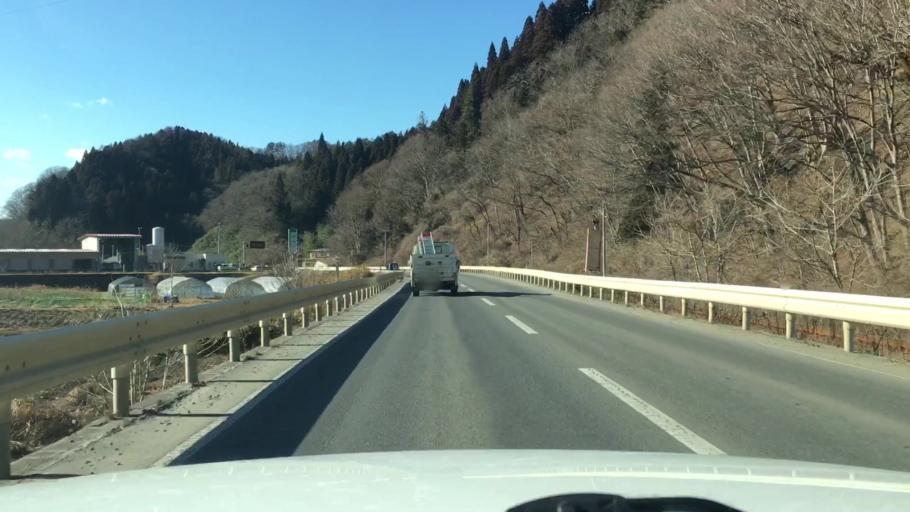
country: JP
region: Iwate
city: Miyako
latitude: 39.6325
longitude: 141.8836
